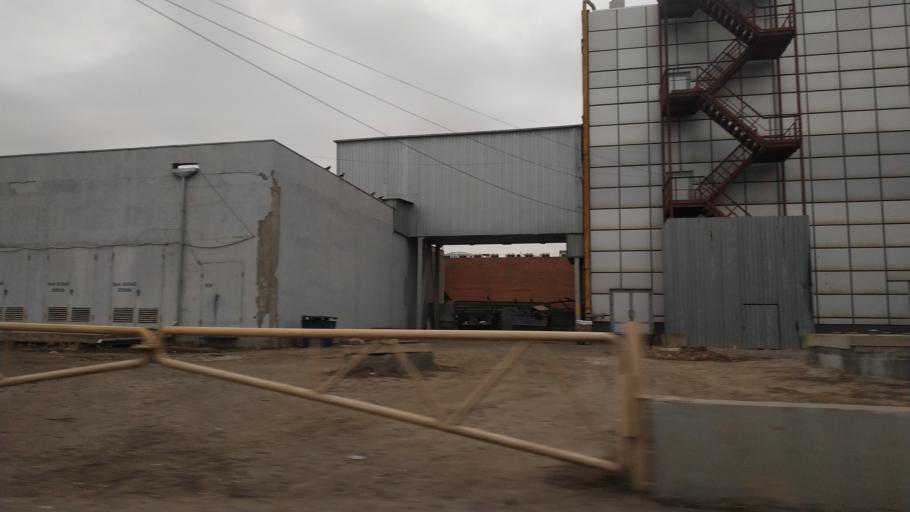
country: RU
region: Astrakhan
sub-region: Gorod Astrakhan'
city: Astrakhan'
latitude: 46.3388
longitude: 48.0255
